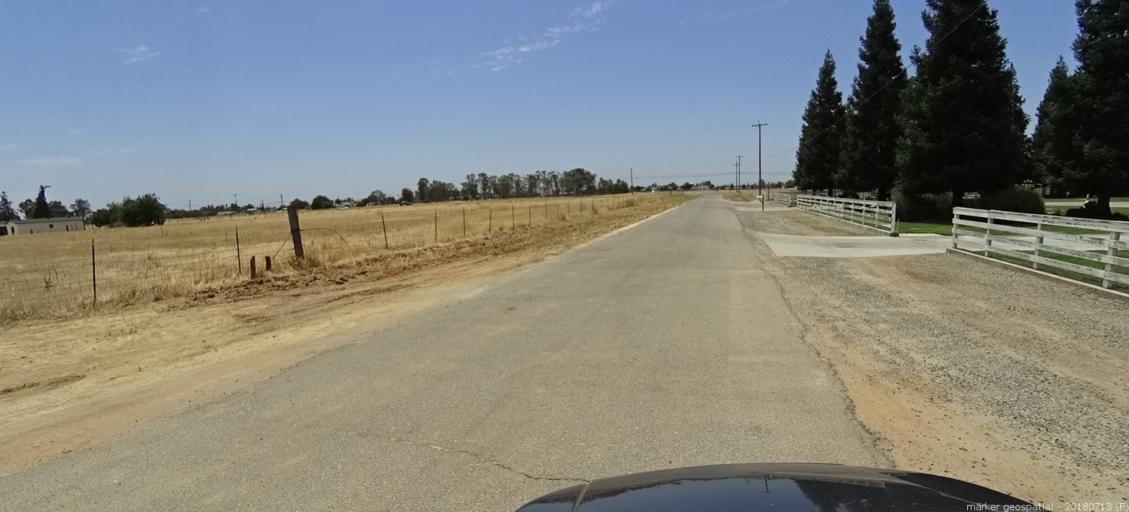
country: US
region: California
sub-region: Madera County
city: Madera Acres
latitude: 36.9982
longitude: -120.0675
